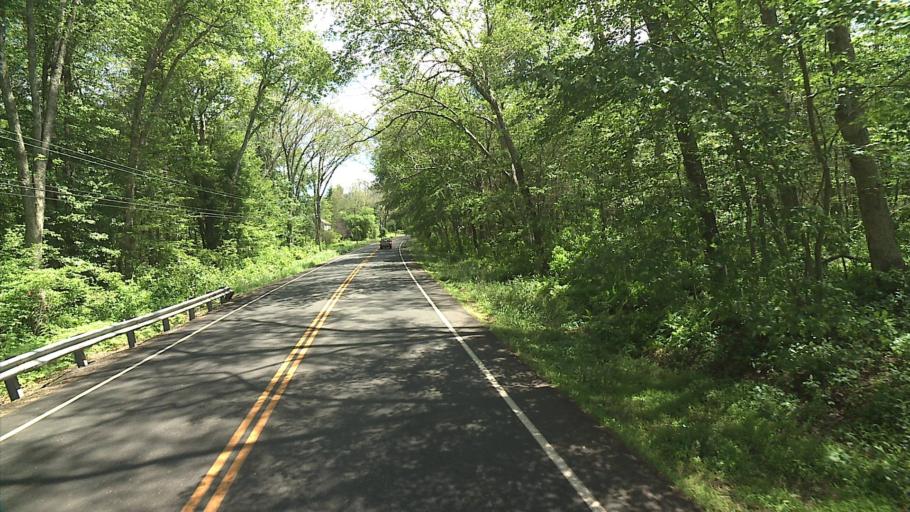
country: US
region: Connecticut
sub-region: Windham County
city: Plainfield
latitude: 41.6028
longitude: -71.8515
